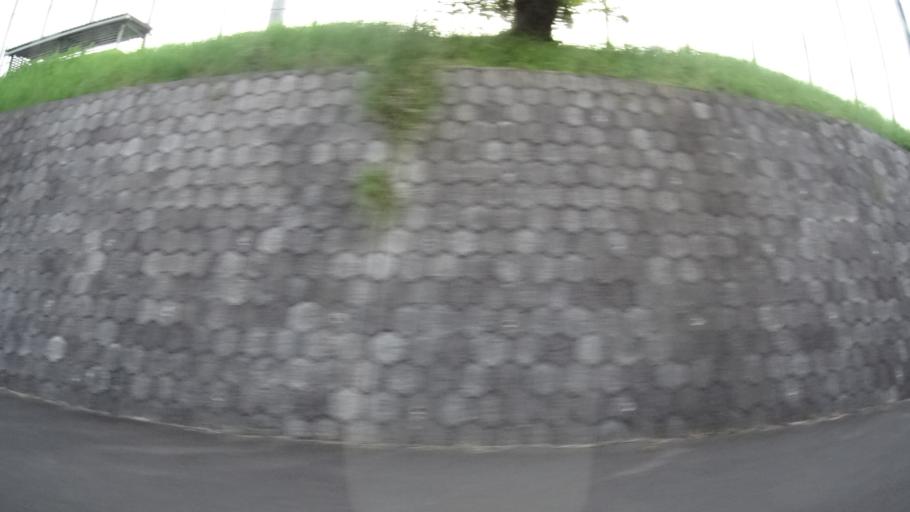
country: JP
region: Tochigi
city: Karasuyama
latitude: 36.6458
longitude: 140.1529
